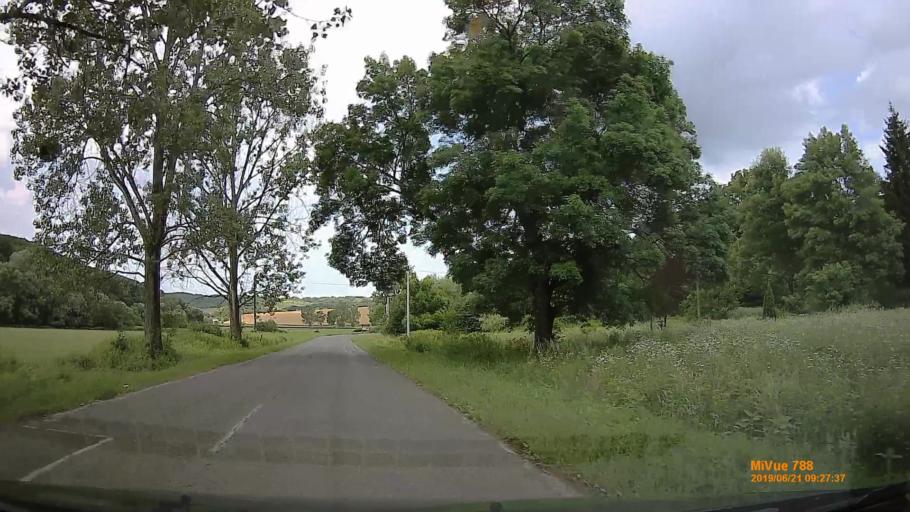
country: HU
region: Somogy
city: Taszar
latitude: 46.2785
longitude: 17.8956
